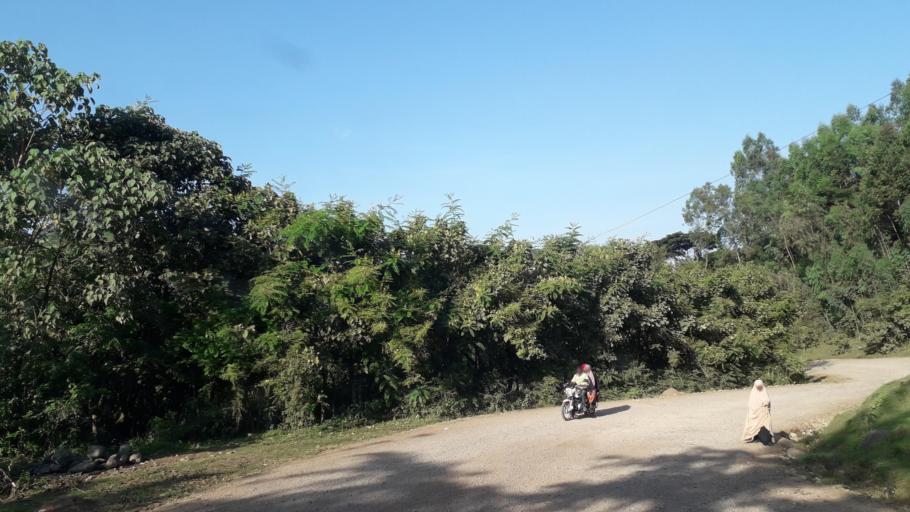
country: ET
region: Oromiya
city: Jima
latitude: 7.4784
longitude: 36.8797
